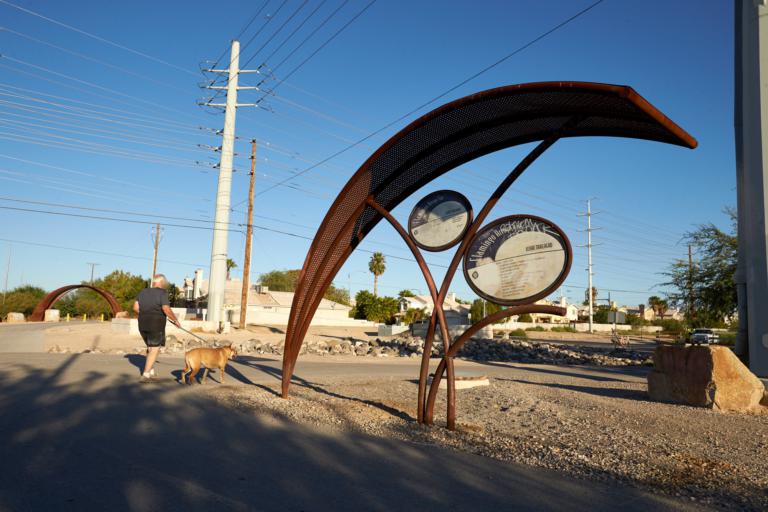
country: US
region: Nevada
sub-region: Clark County
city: Winchester
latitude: 36.1401
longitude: -115.0471
